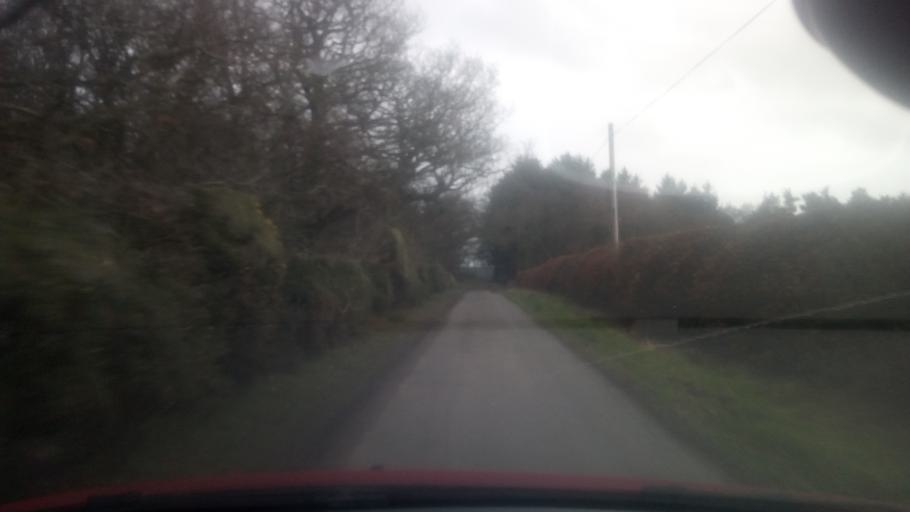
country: GB
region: Scotland
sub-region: The Scottish Borders
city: Jedburgh
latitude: 55.4637
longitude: -2.5198
